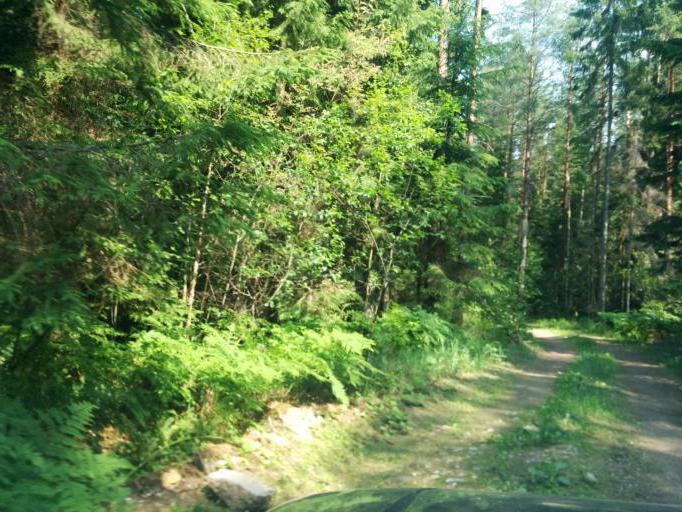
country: LV
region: Ikskile
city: Ikskile
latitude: 56.7442
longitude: 24.4985
